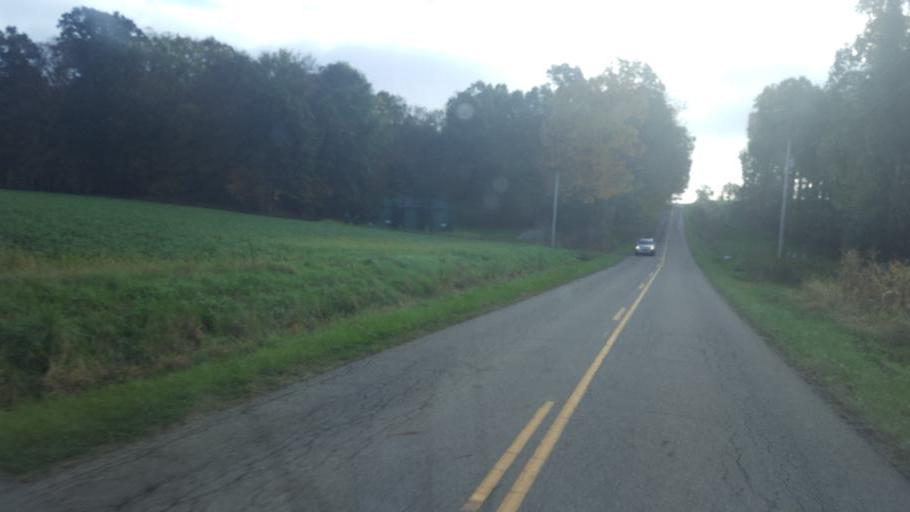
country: US
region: Ohio
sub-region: Knox County
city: Gambier
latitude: 40.4941
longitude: -82.4161
